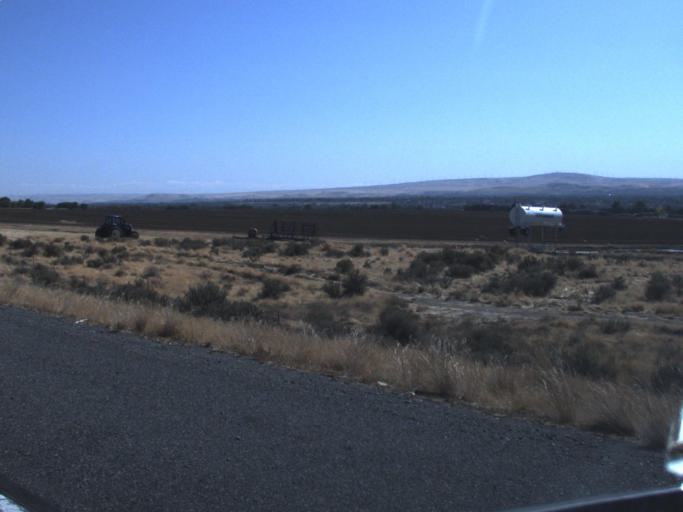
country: US
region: Washington
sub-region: Franklin County
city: West Pasco
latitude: 46.2700
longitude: -119.1971
